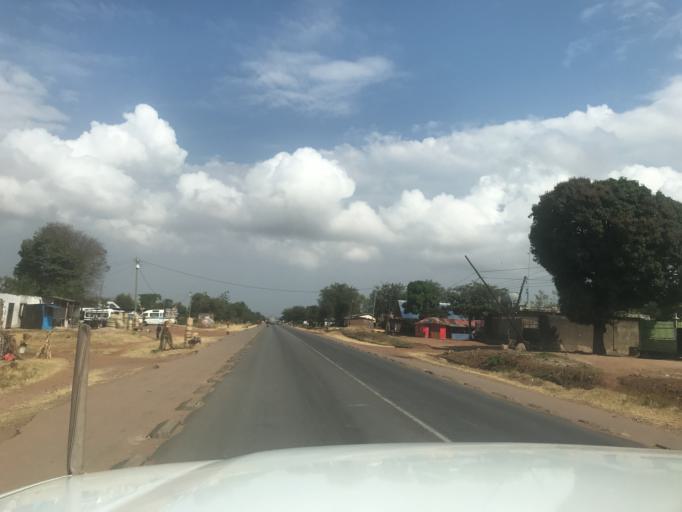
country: TZ
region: Mwanza
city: Usagara
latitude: -2.5554
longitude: 33.0417
